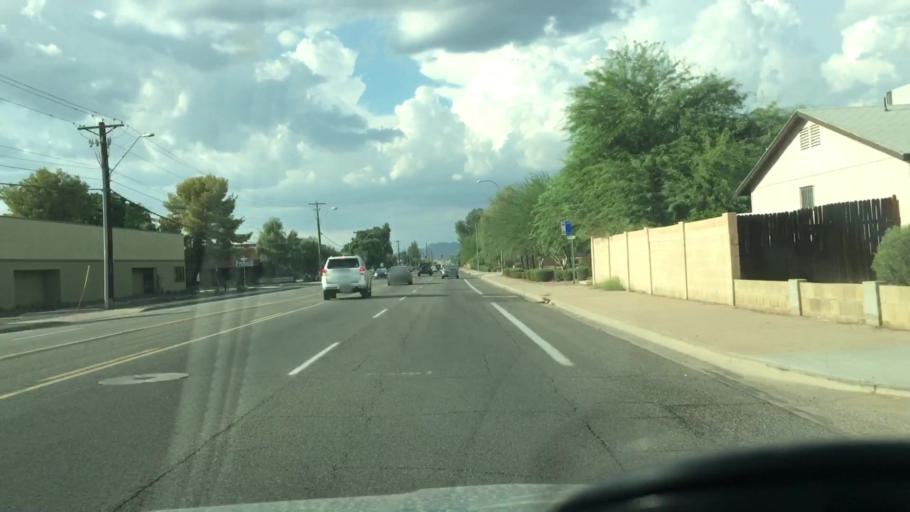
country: US
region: Arizona
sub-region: Maricopa County
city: Guadalupe
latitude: 33.3961
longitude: -111.9955
